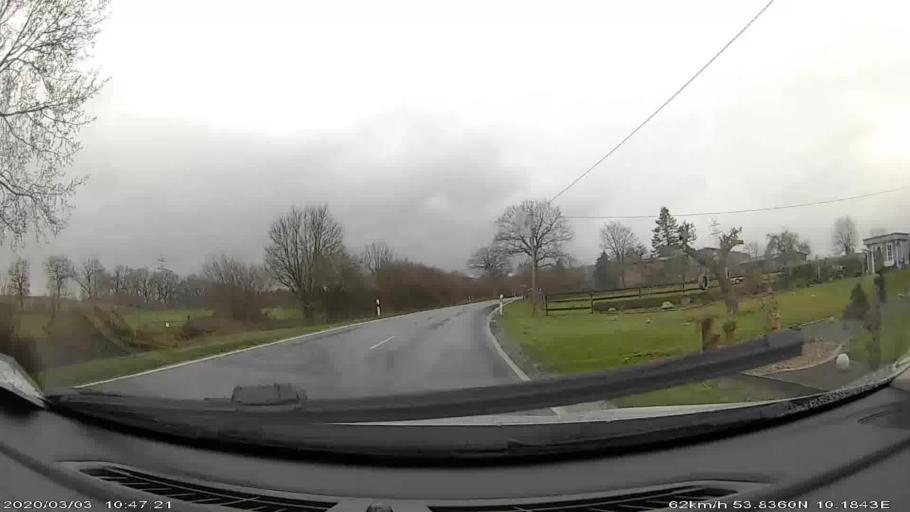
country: DE
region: Schleswig-Holstein
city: Seth
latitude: 53.8331
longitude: 10.1835
